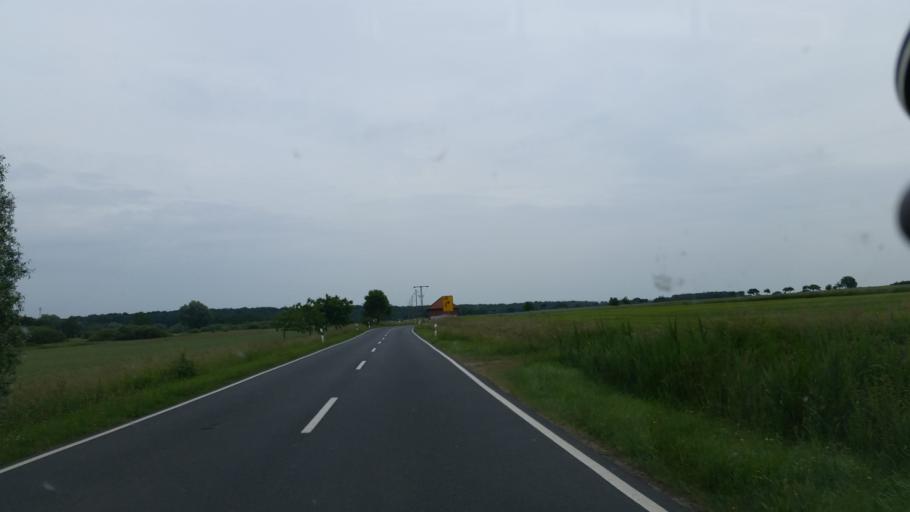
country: DE
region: Lower Saxony
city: Konigslutter am Elm
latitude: 52.2943
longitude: 10.7622
